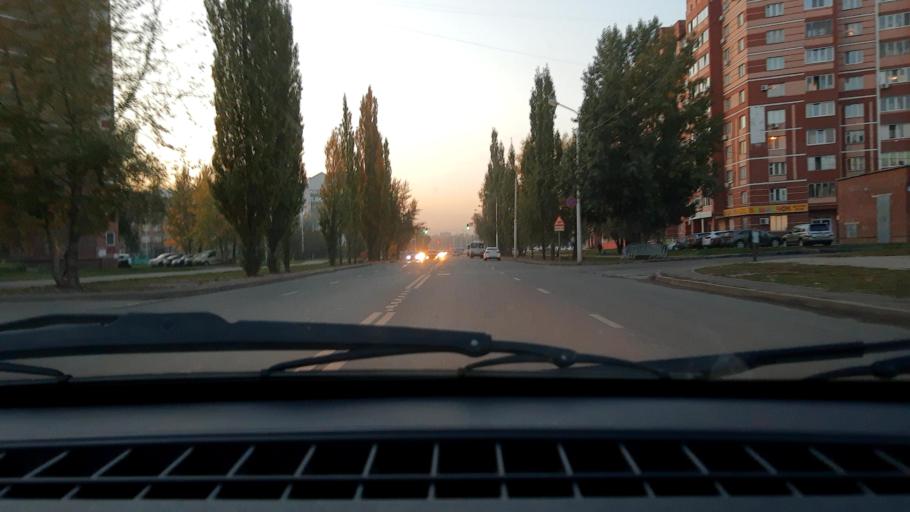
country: RU
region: Bashkortostan
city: Ufa
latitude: 54.7769
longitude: 56.0754
